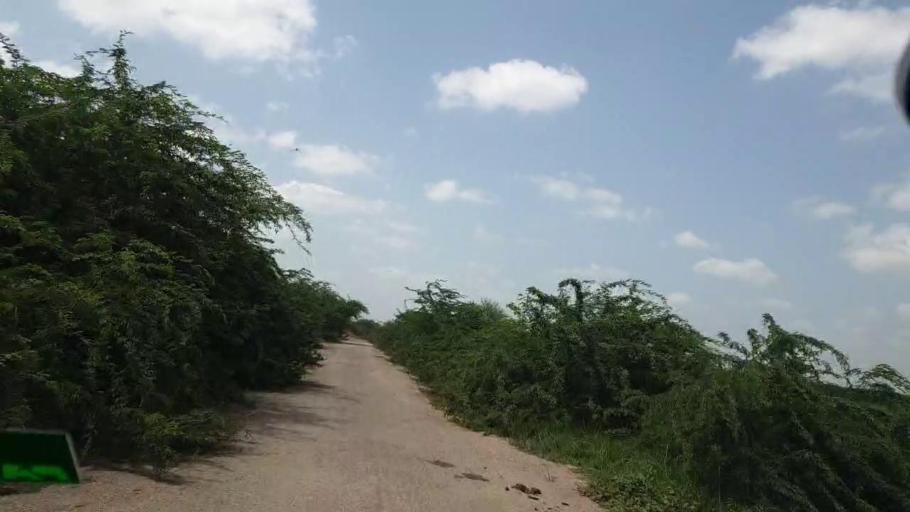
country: PK
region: Sindh
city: Kadhan
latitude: 24.5518
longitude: 69.1953
